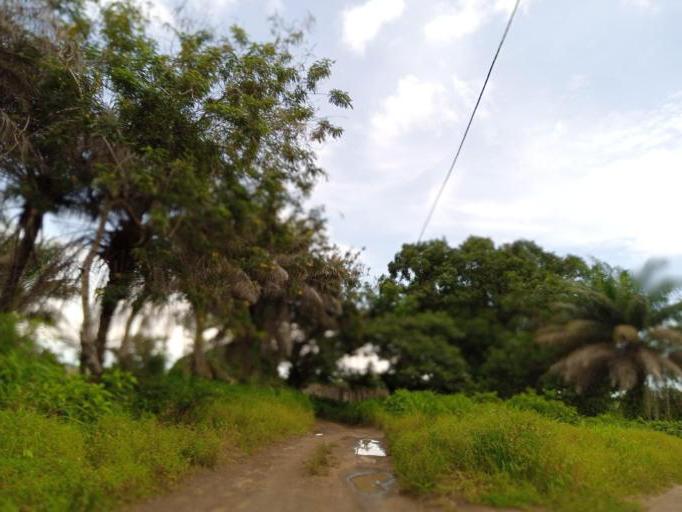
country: SL
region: Northern Province
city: Masoyila
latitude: 8.5922
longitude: -13.1691
